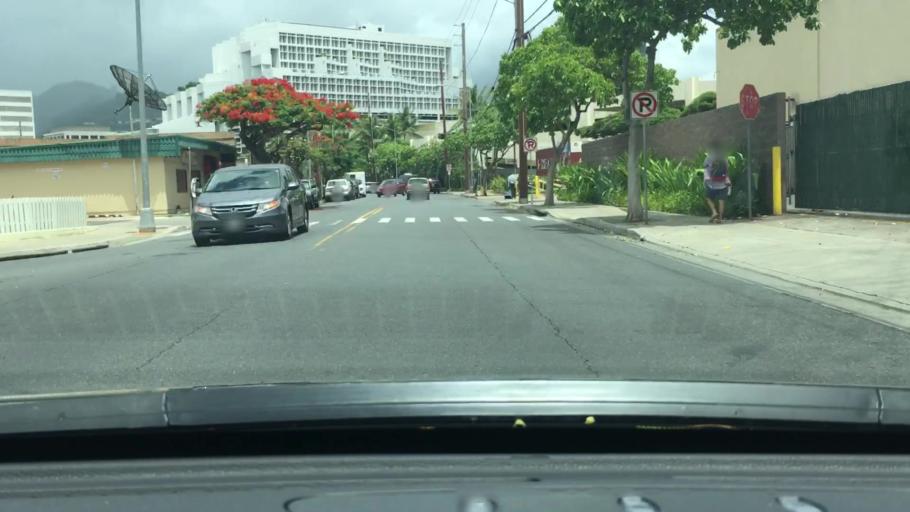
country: US
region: Hawaii
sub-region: Honolulu County
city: Honolulu
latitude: 21.2955
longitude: -157.8437
